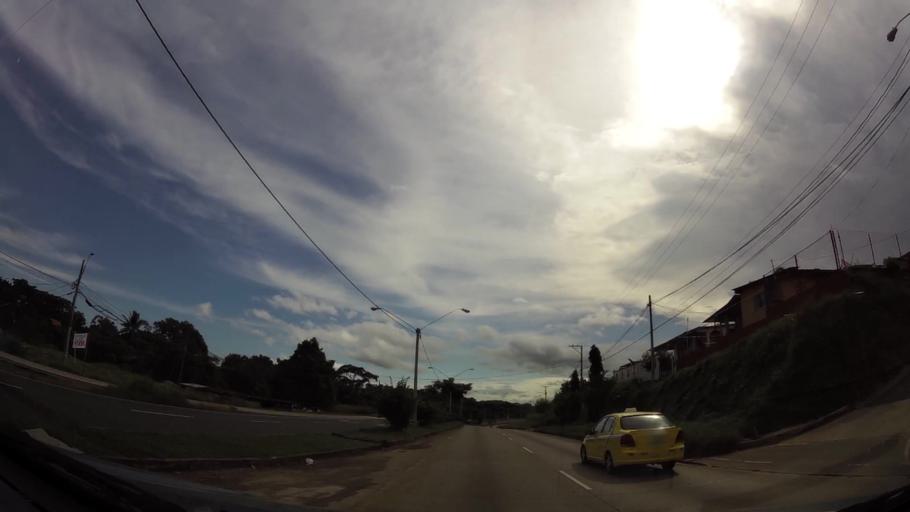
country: PA
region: Panama
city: El Coco
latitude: 8.8676
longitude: -79.8025
